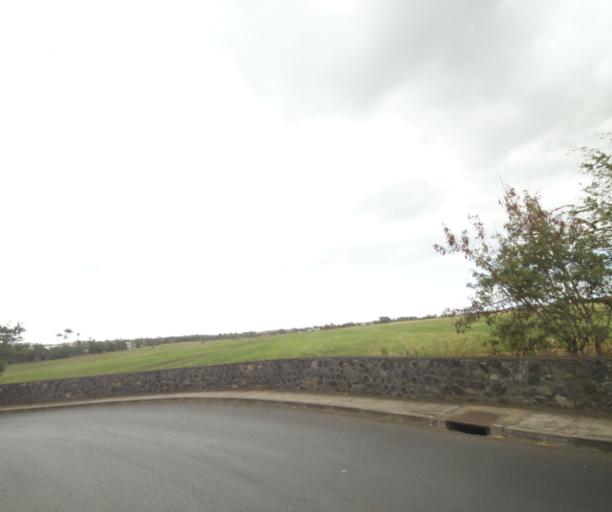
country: RE
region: Reunion
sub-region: Reunion
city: Saint-Paul
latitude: -20.9851
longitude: 55.2985
